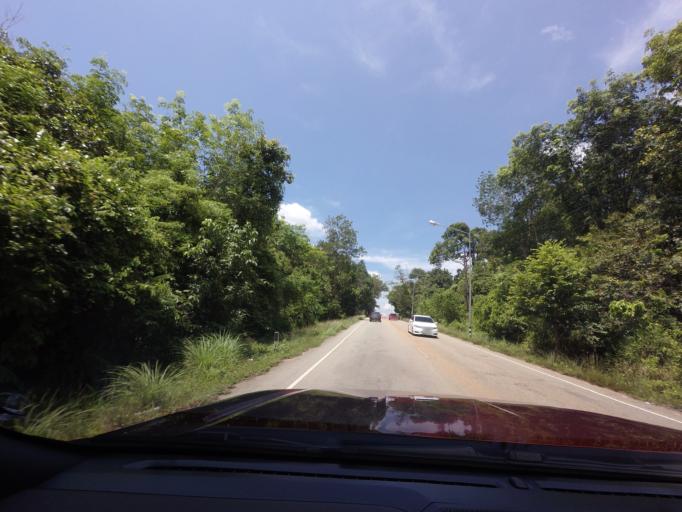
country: TH
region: Narathiwat
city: Chanae
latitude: 6.1834
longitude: 101.6964
